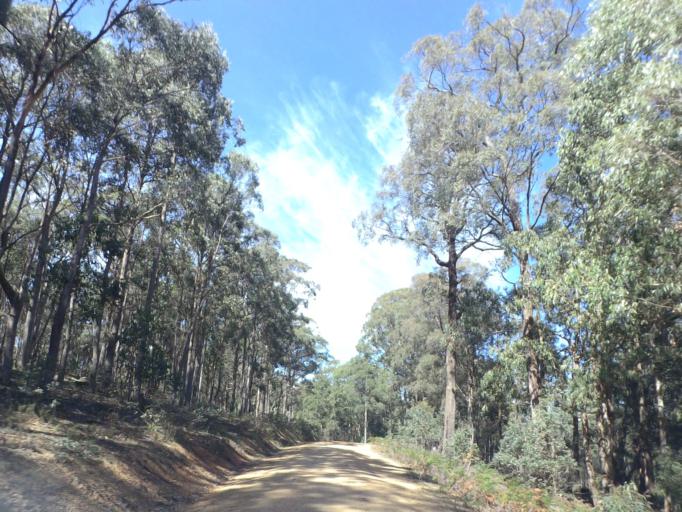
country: AU
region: Victoria
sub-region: Moorabool
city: Bacchus Marsh
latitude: -37.4352
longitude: 144.3624
